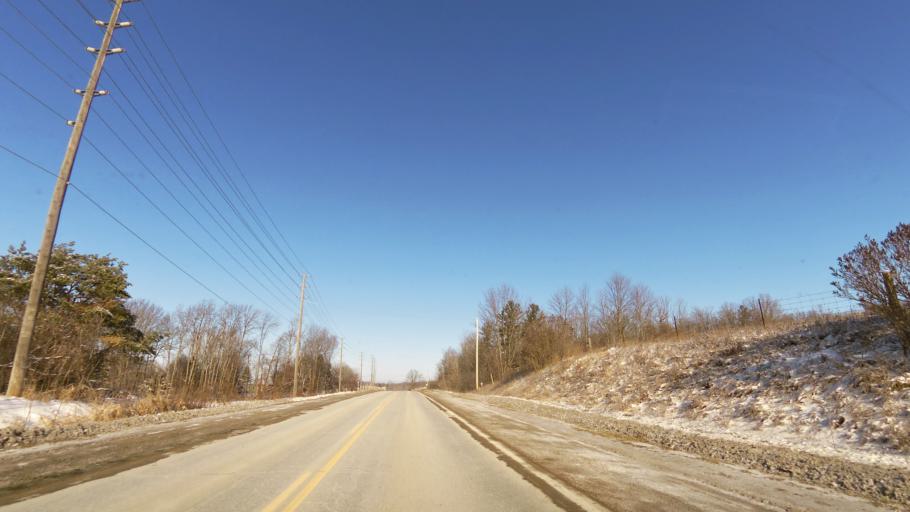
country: CA
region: Ontario
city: Quinte West
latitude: 44.2050
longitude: -77.8218
